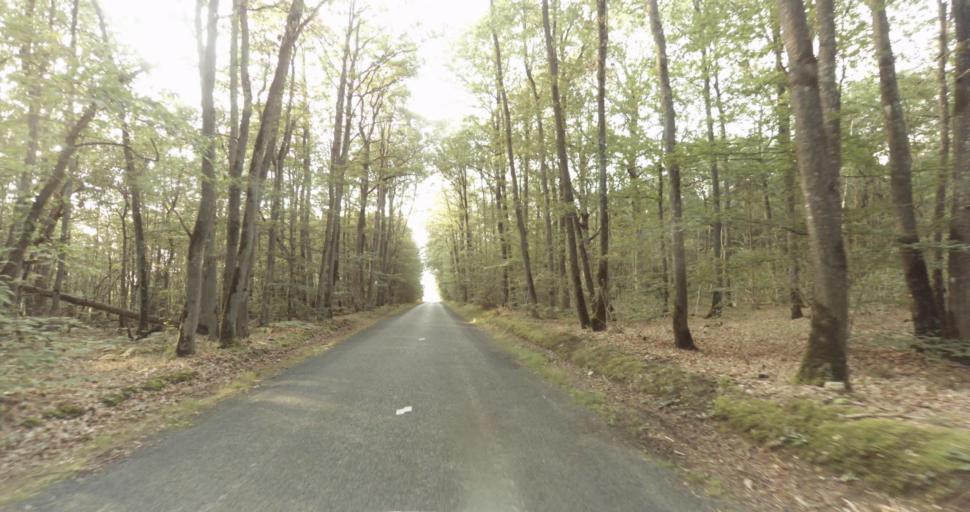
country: FR
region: Haute-Normandie
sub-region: Departement de l'Eure
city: Marcilly-sur-Eure
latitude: 48.8125
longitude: 1.2993
